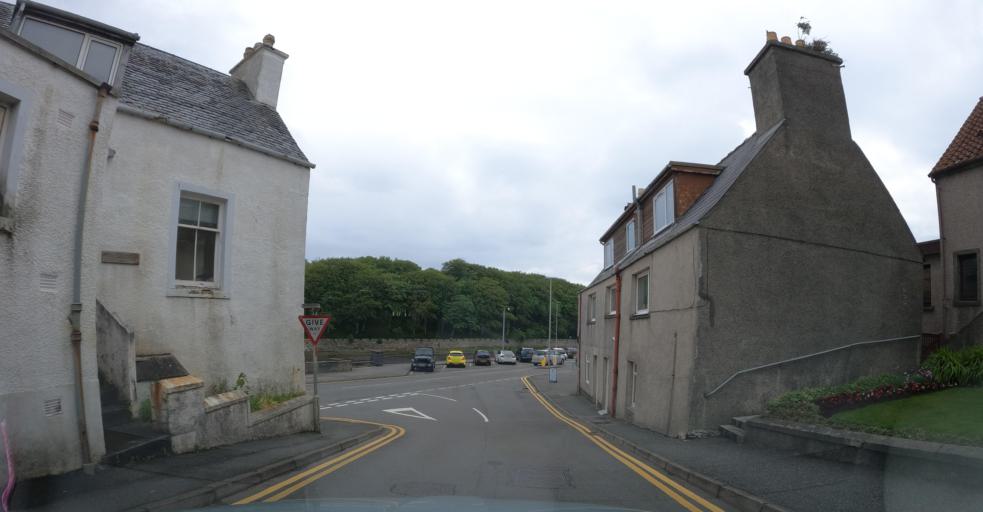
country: GB
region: Scotland
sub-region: Eilean Siar
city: Stornoway
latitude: 58.2112
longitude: -6.3884
